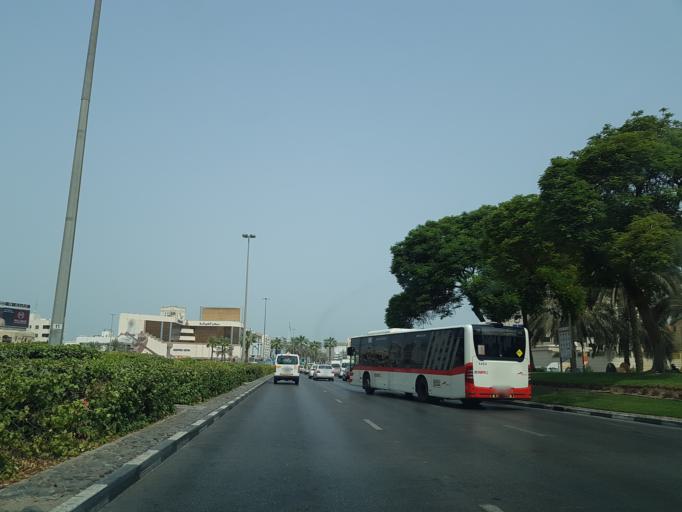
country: AE
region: Ash Shariqah
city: Sharjah
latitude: 25.2342
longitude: 55.2802
